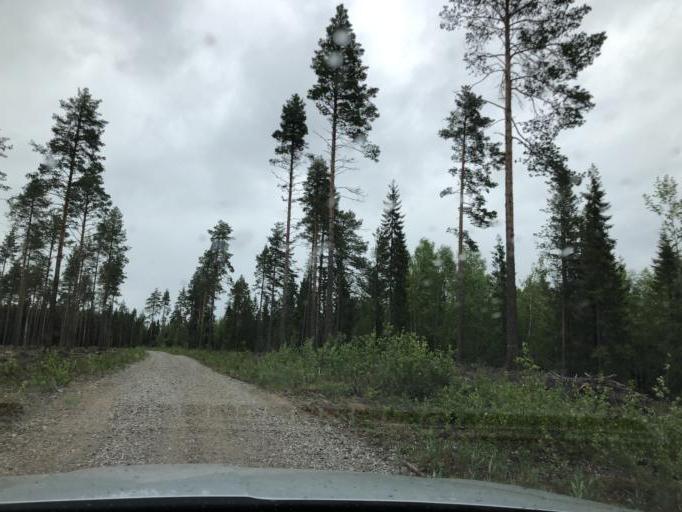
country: SE
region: Norrbotten
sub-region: Pitea Kommun
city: Roknas
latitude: 65.3974
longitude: 21.2703
